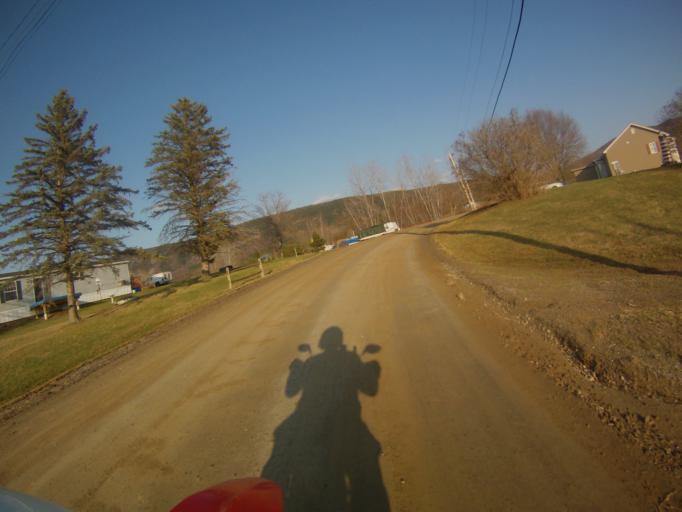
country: US
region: Vermont
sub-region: Addison County
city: Bristol
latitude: 44.0920
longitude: -73.0972
